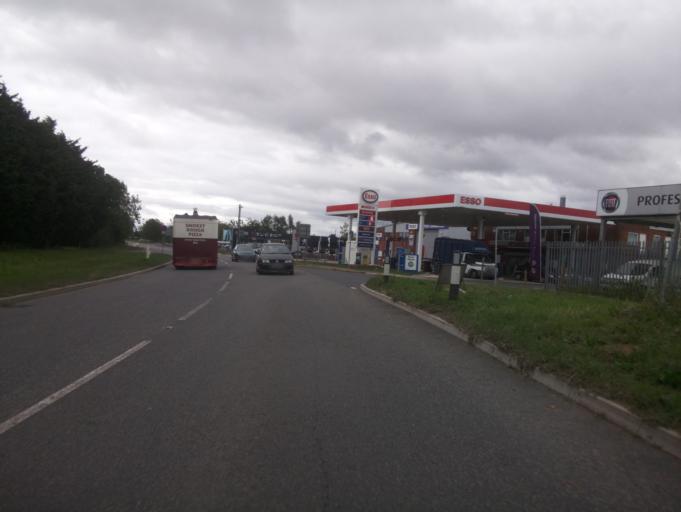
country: GB
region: England
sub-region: Worcestershire
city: Kempsey
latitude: 52.1615
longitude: -2.2164
